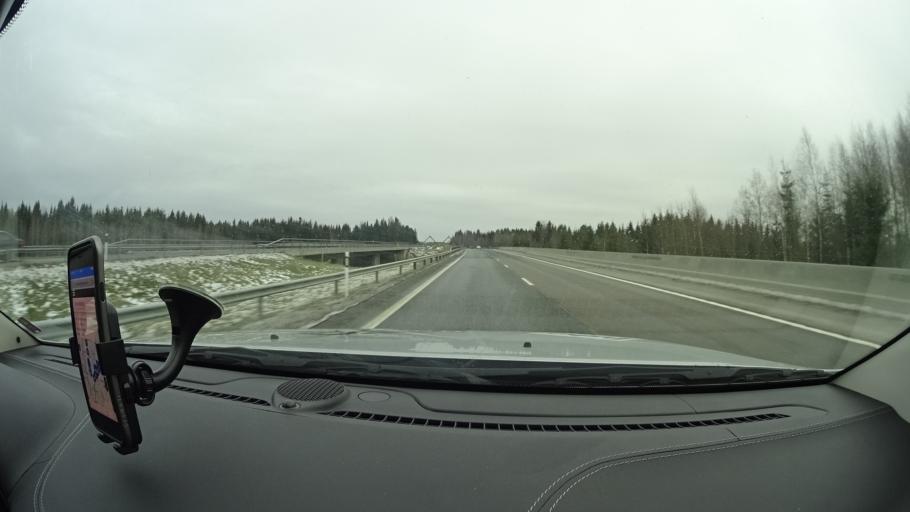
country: FI
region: Paijanne Tavastia
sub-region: Lahti
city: Nastola
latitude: 61.0815
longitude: 25.8927
